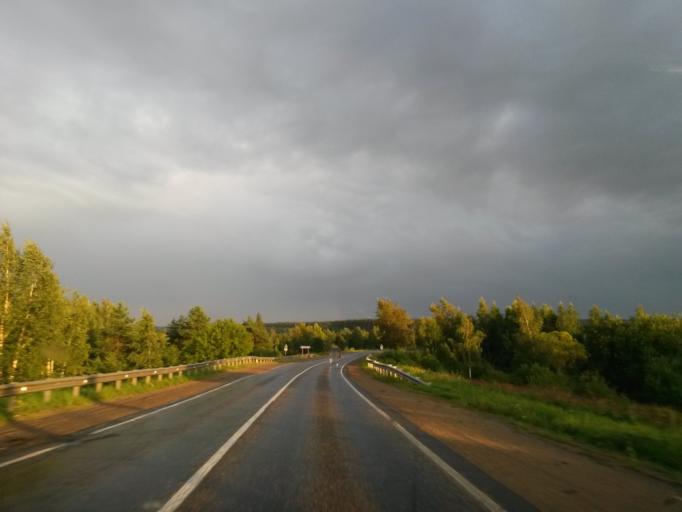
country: RU
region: Jaroslavl
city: Yaroslavl
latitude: 57.5150
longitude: 39.8956
